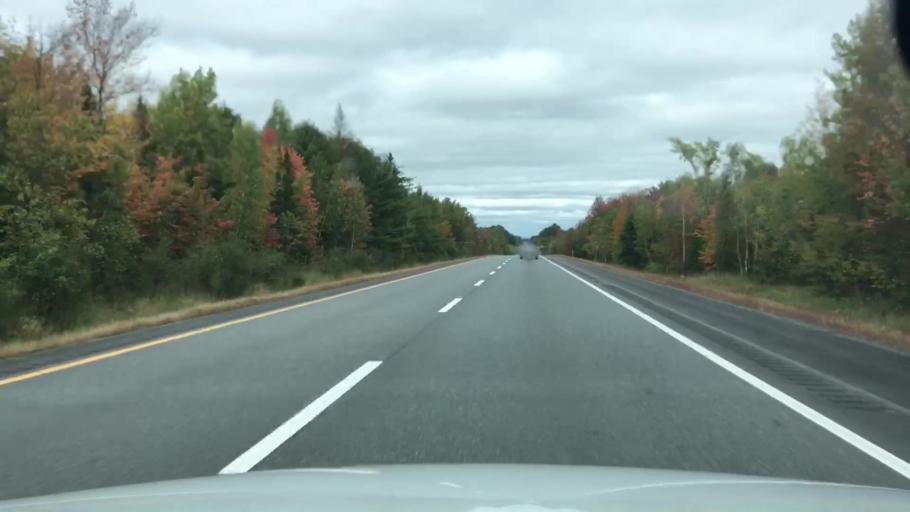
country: US
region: Maine
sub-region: Waldo County
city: Burnham
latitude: 44.7364
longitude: -69.4317
